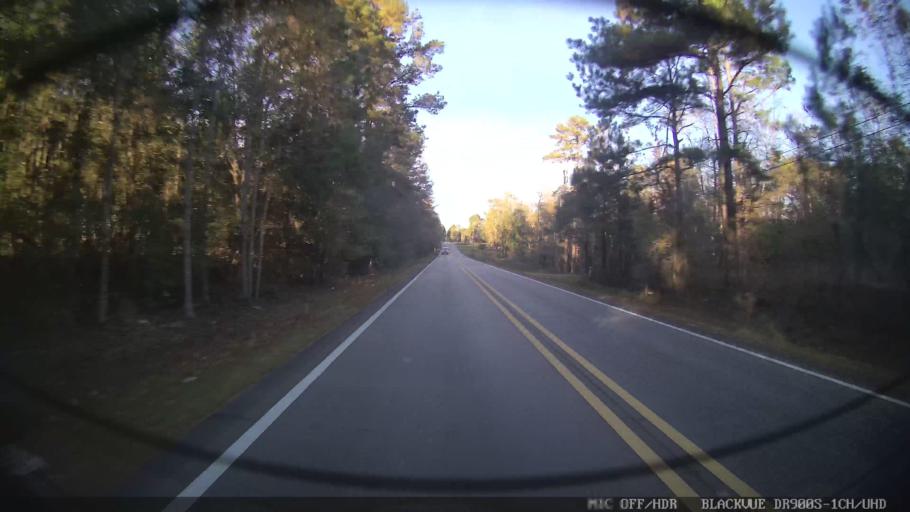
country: US
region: Mississippi
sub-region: Lamar County
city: Lumberton
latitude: 31.0447
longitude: -89.4358
